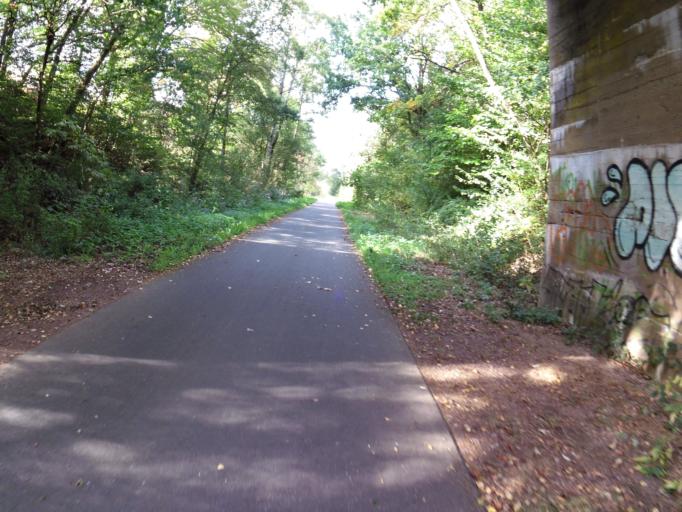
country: DE
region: Rheinland-Pfalz
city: Bleialf
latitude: 50.2192
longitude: 6.2701
